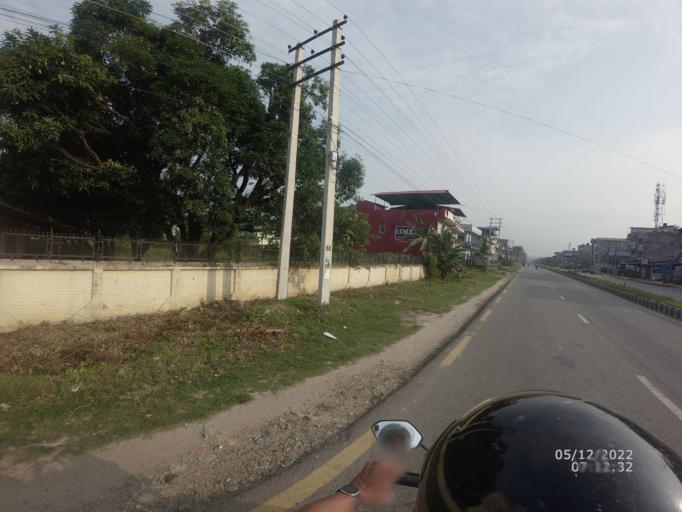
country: NP
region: Central Region
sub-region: Narayani Zone
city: Bharatpur
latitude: 27.6855
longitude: 84.4397
